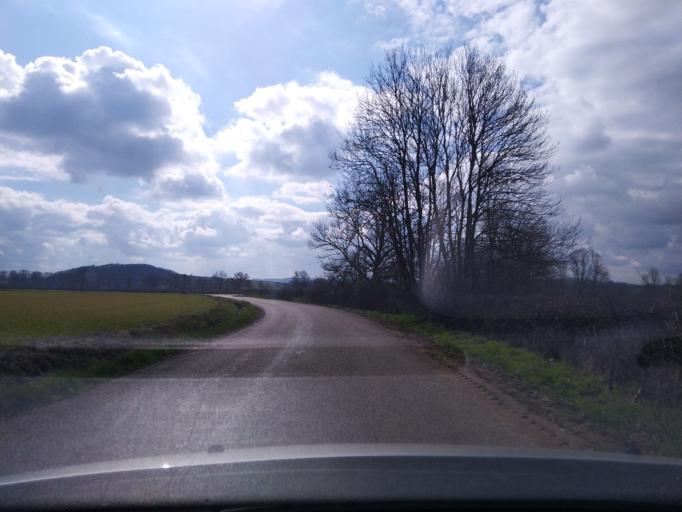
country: FR
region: Bourgogne
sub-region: Departement de l'Yonne
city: Avallon
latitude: 47.5513
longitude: 4.0554
